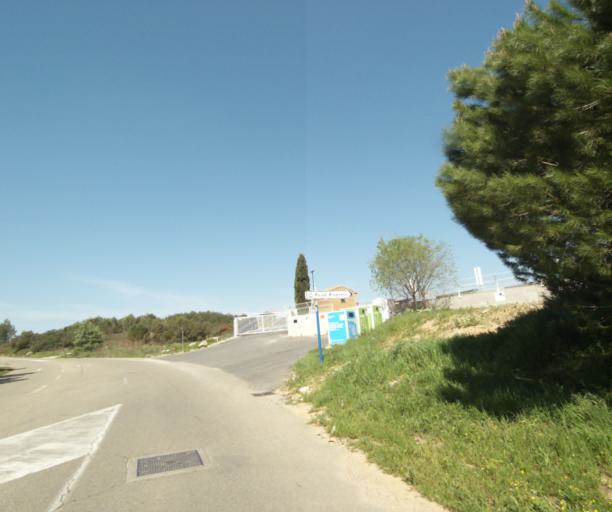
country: FR
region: Languedoc-Roussillon
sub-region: Departement de l'Herault
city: Castries
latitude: 43.6672
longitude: 3.9956
